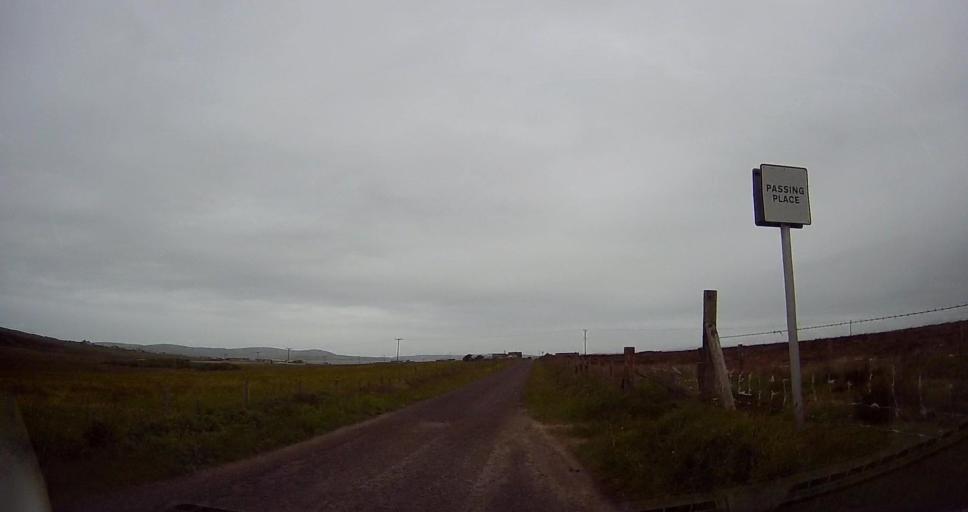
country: GB
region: Scotland
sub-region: Orkney Islands
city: Stromness
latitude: 58.9835
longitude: -3.1851
